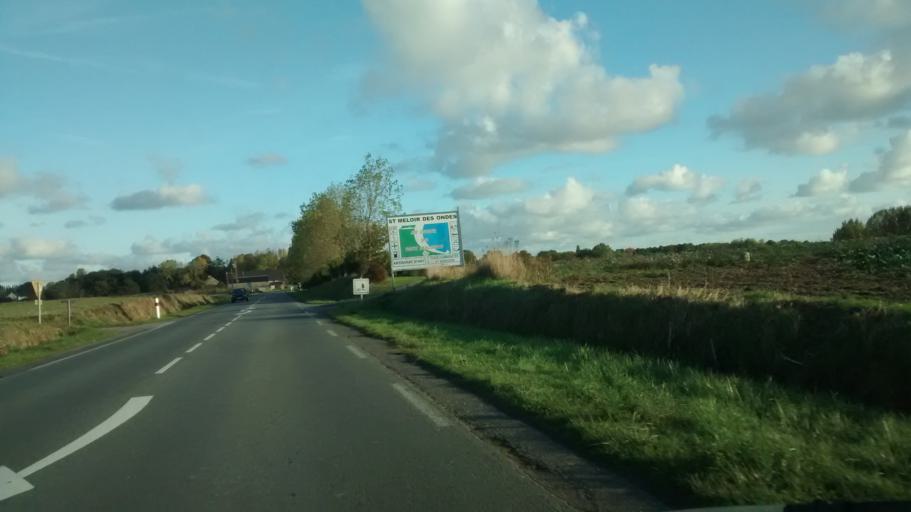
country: FR
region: Brittany
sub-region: Departement d'Ille-et-Vilaine
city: Saint-Meloir-des-Ondes
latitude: 48.6251
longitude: -1.9045
